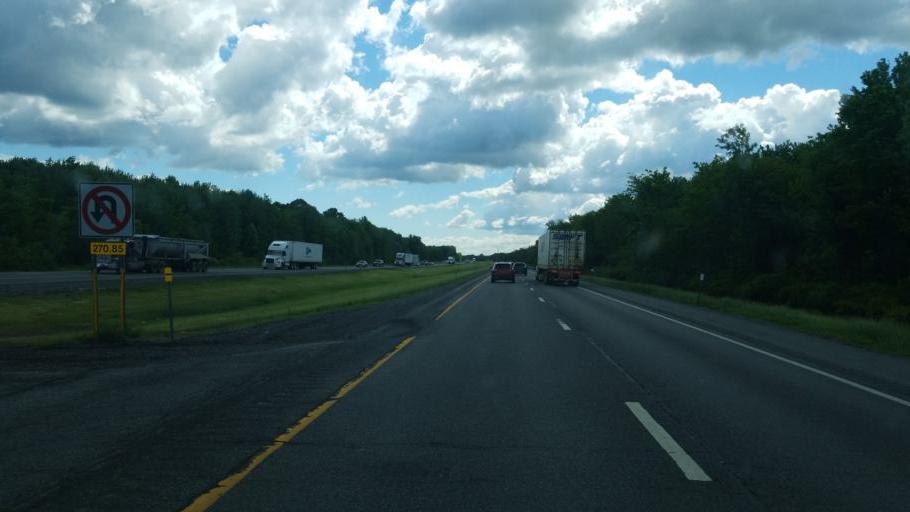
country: US
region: New York
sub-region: Madison County
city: Bolivar
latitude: 43.0913
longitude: -75.9316
